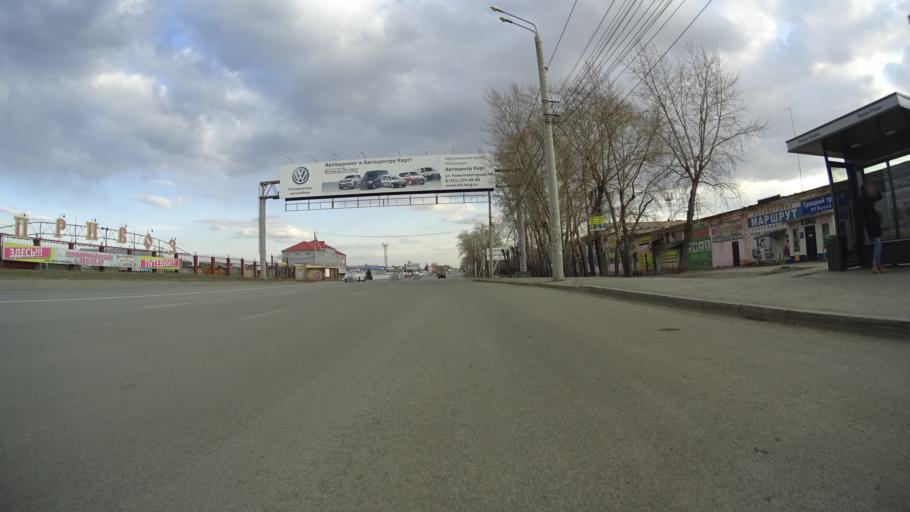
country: RU
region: Chelyabinsk
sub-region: Gorod Chelyabinsk
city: Chelyabinsk
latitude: 55.1104
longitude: 61.3867
